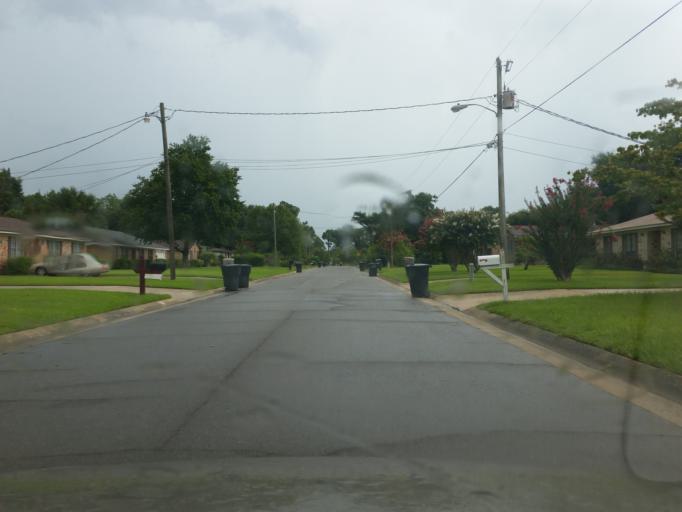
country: US
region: Florida
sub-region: Escambia County
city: Ferry Pass
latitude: 30.4904
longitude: -87.2174
